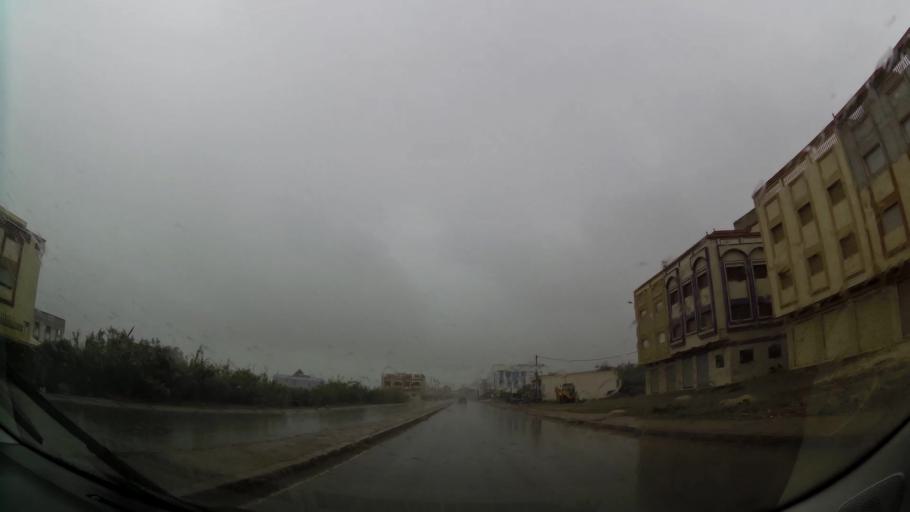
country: MA
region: Taza-Al Hoceima-Taounate
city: Imzourene
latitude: 35.1201
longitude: -3.8431
